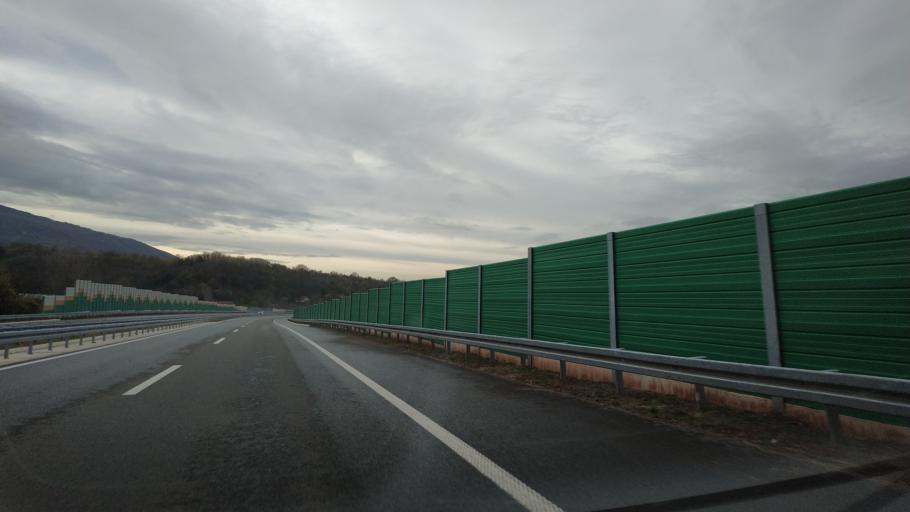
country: RS
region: Central Serbia
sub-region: Nisavski Okrug
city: Niska Banja
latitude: 43.3007
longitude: 22.0552
